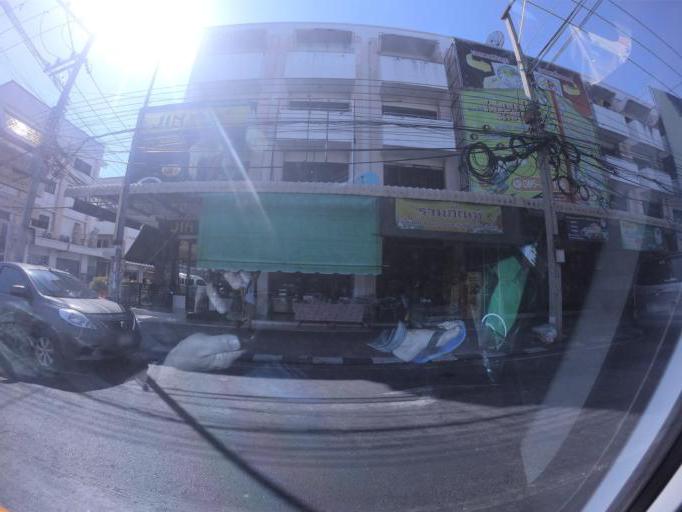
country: TH
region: Khon Kaen
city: Khon Kaen
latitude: 16.4263
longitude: 102.8351
